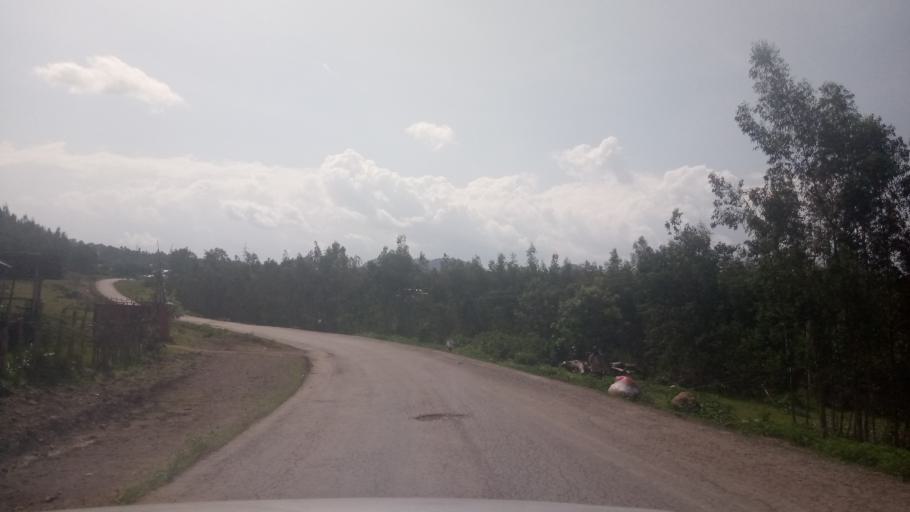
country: ET
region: Oromiya
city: Agaro
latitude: 7.9954
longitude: 36.5039
